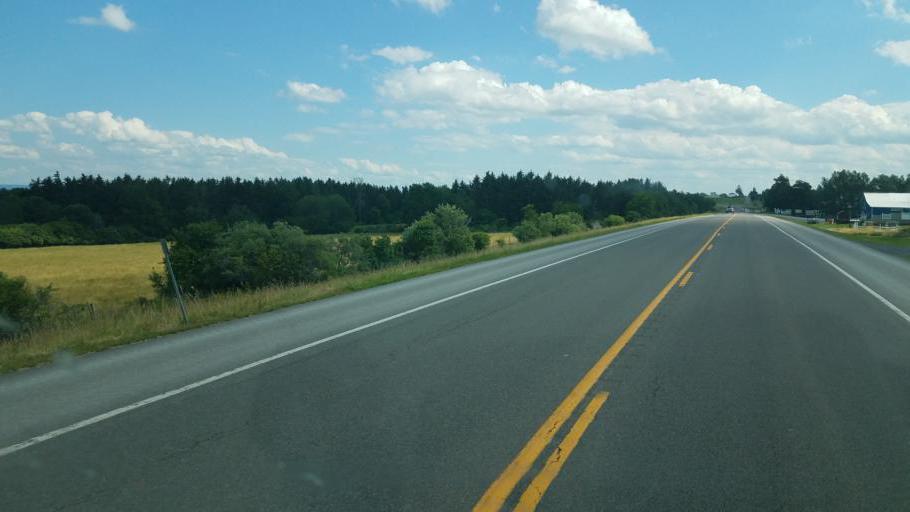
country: US
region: New York
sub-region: Yates County
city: Dundee
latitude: 42.5673
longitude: -77.0355
